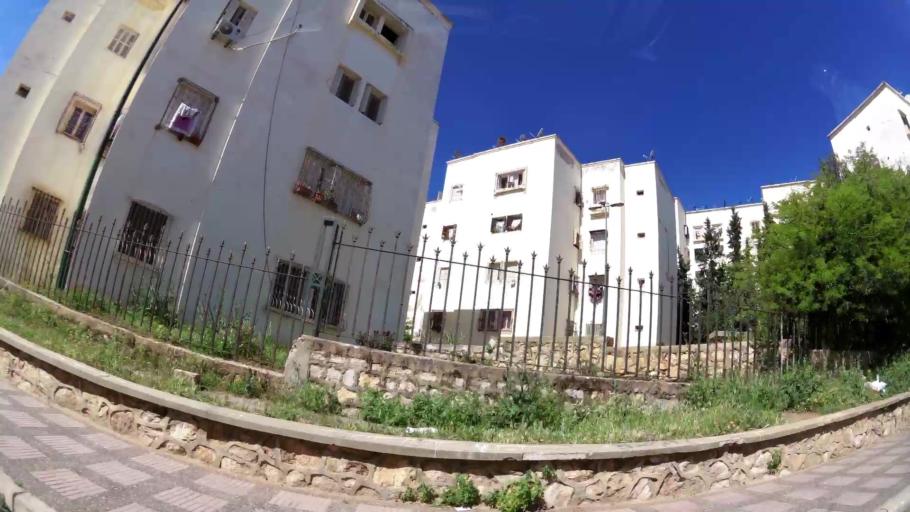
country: MA
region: Meknes-Tafilalet
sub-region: Meknes
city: Meknes
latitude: 33.9092
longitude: -5.5418
